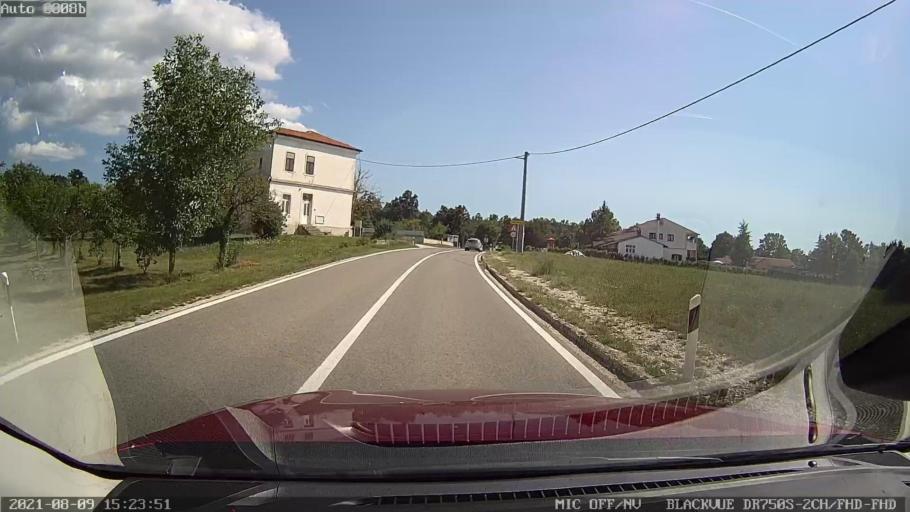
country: HR
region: Istarska
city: Pazin
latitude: 45.1799
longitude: 13.9044
